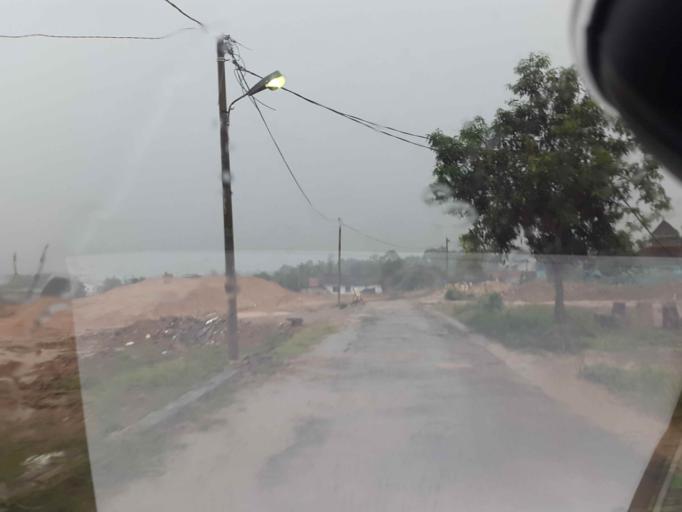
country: ID
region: Lampung
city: Panjang
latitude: -5.3984
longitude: 105.3535
